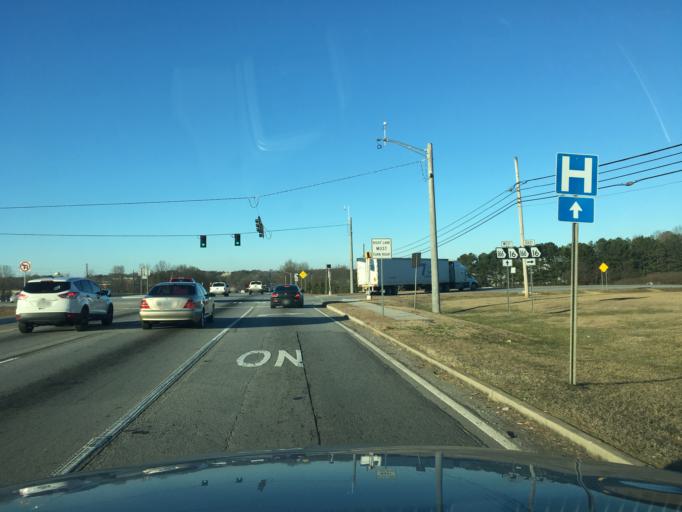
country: US
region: Georgia
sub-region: Carroll County
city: Carrollton
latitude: 33.5560
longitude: -85.0730
